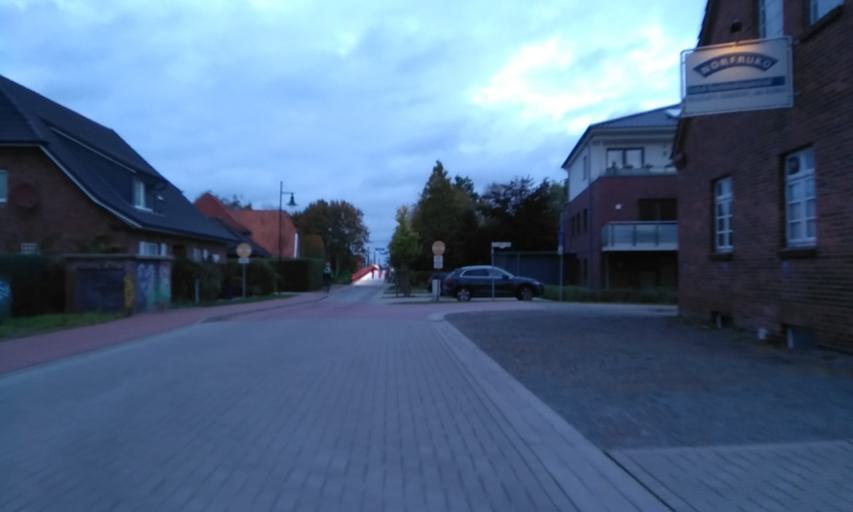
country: DE
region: Lower Saxony
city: Harsefeld
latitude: 53.4483
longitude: 9.4988
